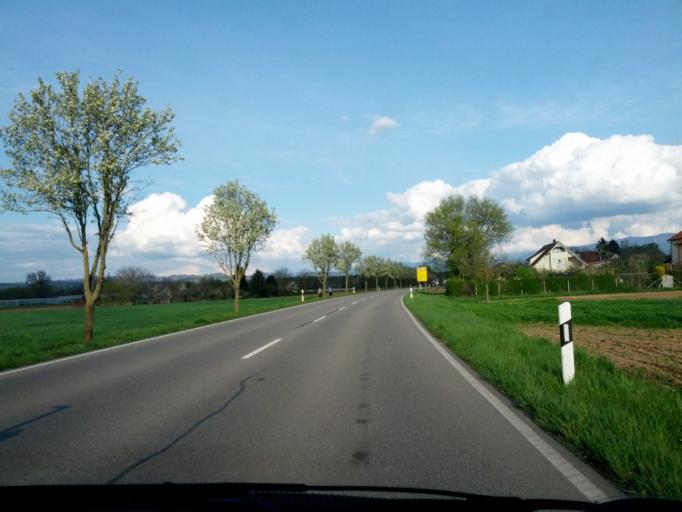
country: DE
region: Baden-Wuerttemberg
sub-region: Freiburg Region
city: Eichstetten
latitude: 48.1077
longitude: 7.7716
